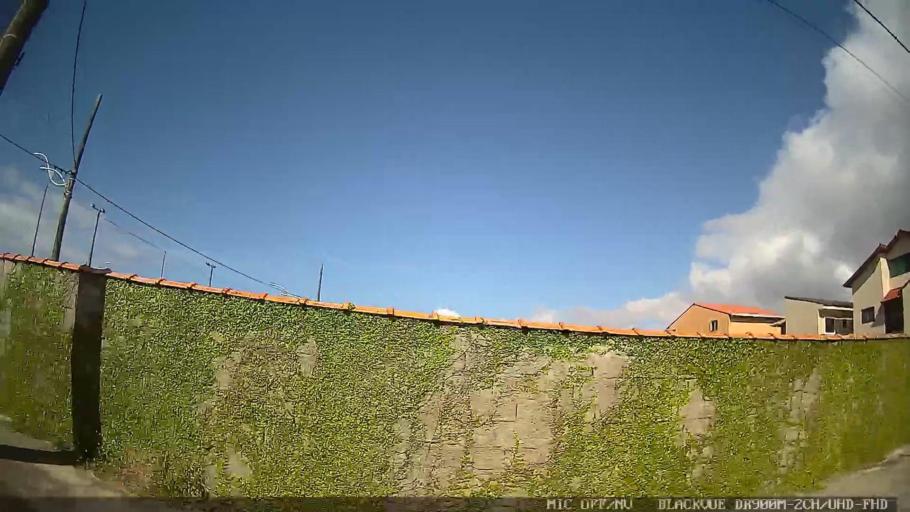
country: BR
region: Sao Paulo
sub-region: Peruibe
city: Peruibe
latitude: -24.2873
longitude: -46.9521
